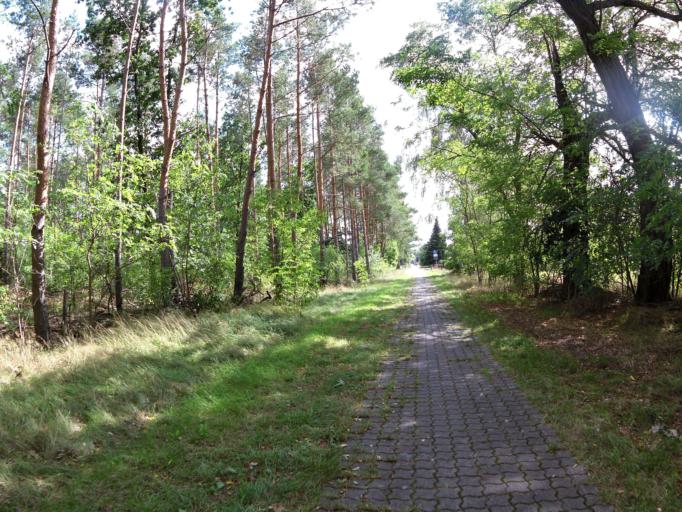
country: DE
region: Brandenburg
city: Storkow
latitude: 52.2206
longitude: 13.8730
